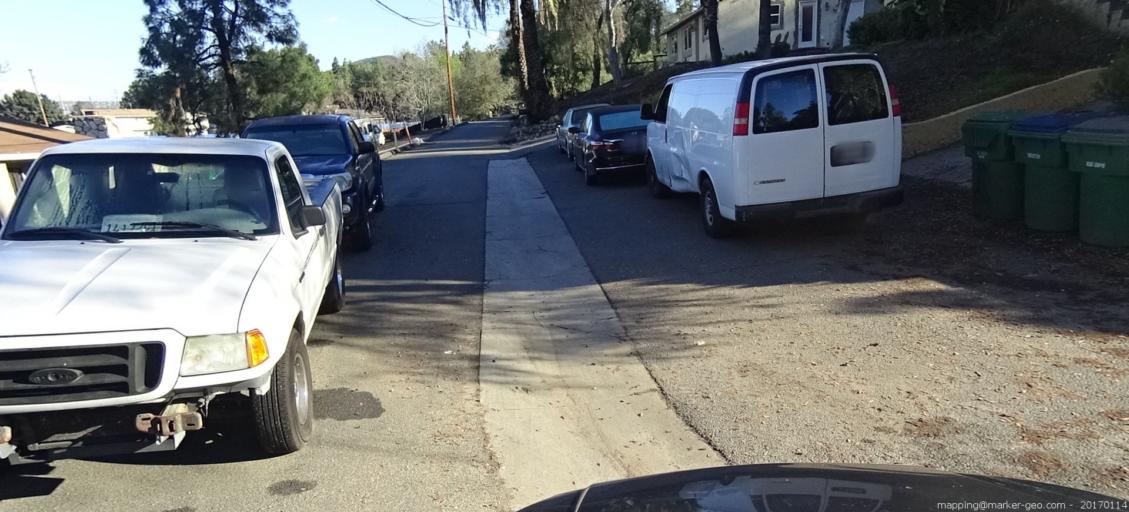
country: US
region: California
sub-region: Orange County
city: North Tustin
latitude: 33.7844
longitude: -117.8029
